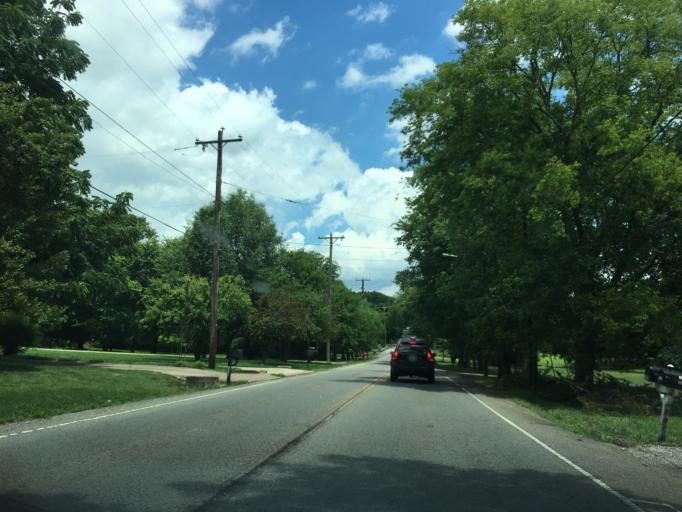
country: US
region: Tennessee
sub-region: Davidson County
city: Oak Hill
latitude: 36.0891
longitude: -86.8003
